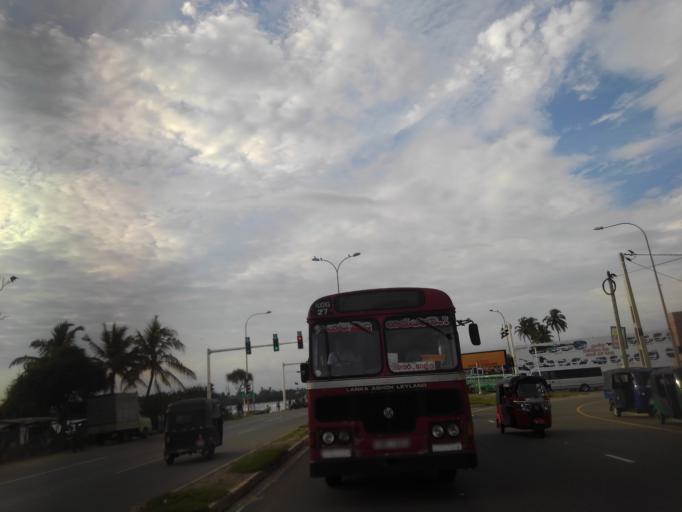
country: LK
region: Southern
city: Unawatuna
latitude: 6.0293
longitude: 80.2423
